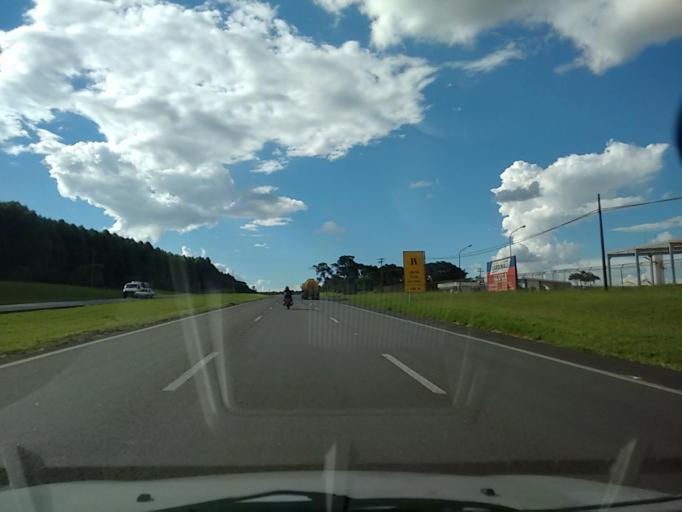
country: BR
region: Sao Paulo
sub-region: Sao Carlos
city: Sao Carlos
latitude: -22.0541
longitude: -47.8559
